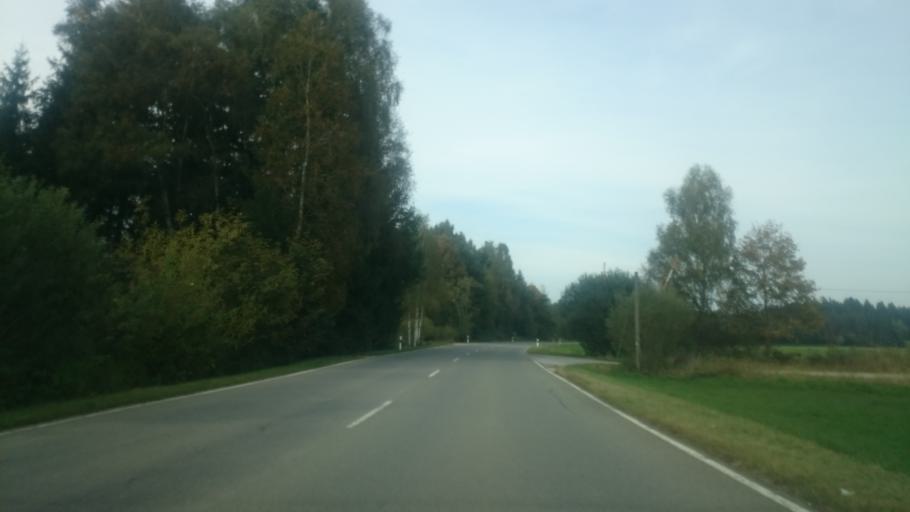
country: AT
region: Tyrol
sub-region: Politischer Bezirk Reutte
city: Vils
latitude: 47.5778
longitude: 10.6534
